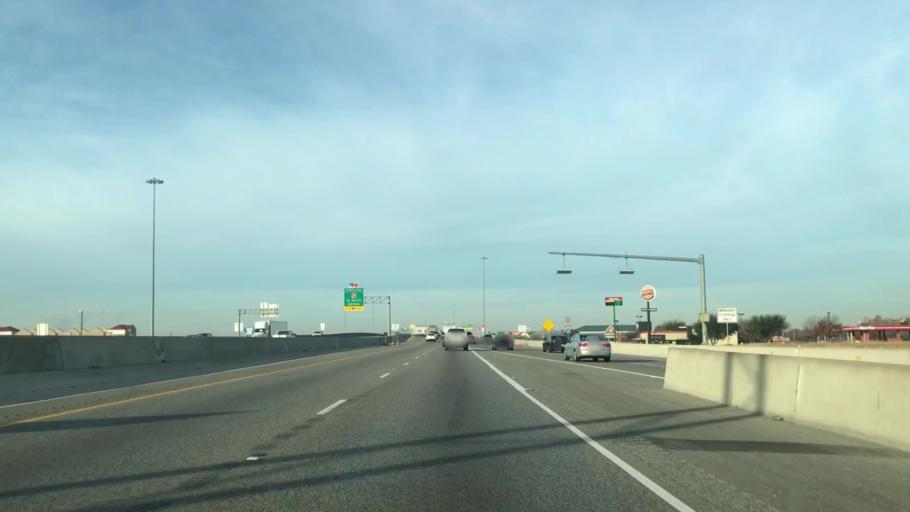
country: US
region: Texas
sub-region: Tarrant County
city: Watauga
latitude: 32.8398
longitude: -97.2871
